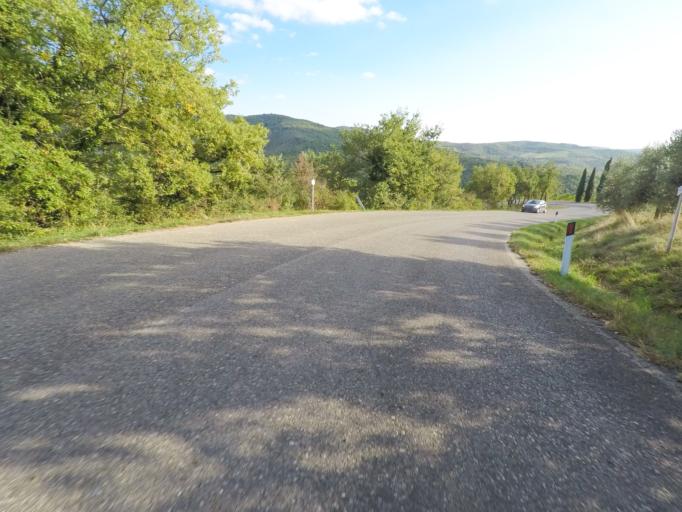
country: IT
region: Tuscany
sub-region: Provincia di Siena
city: Radda in Chianti
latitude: 43.5167
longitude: 11.4056
